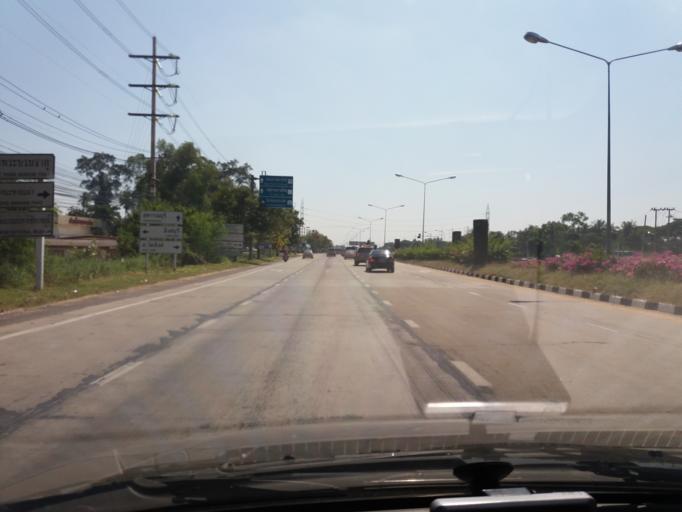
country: TH
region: Chai Nat
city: Chai Nat
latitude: 15.1634
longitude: 100.1446
